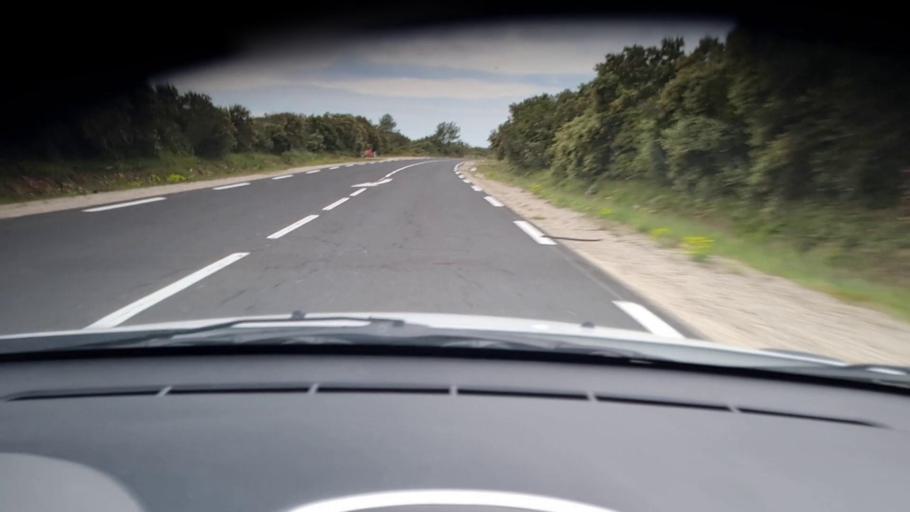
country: FR
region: Languedoc-Roussillon
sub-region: Departement du Gard
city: Poulx
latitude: 43.8984
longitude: 4.3948
